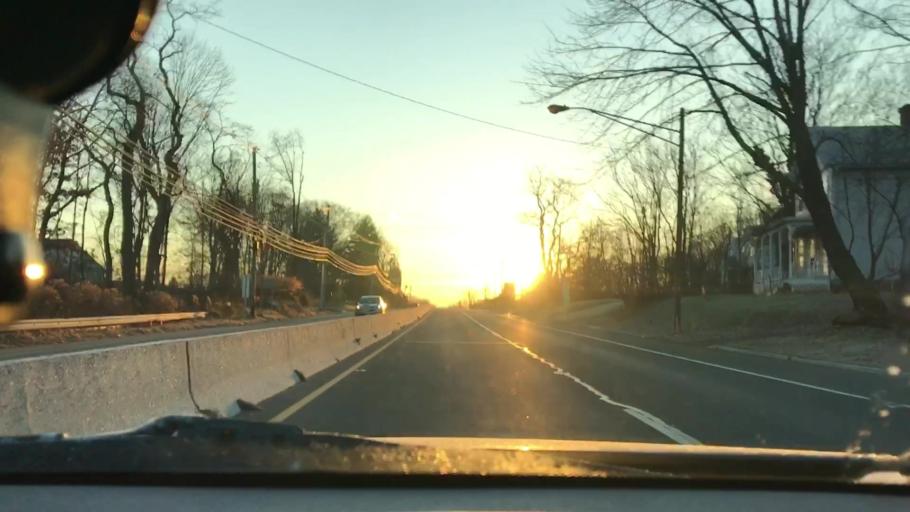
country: US
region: New Jersey
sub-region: Morris County
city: Parsippany
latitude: 40.8284
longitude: -74.4299
